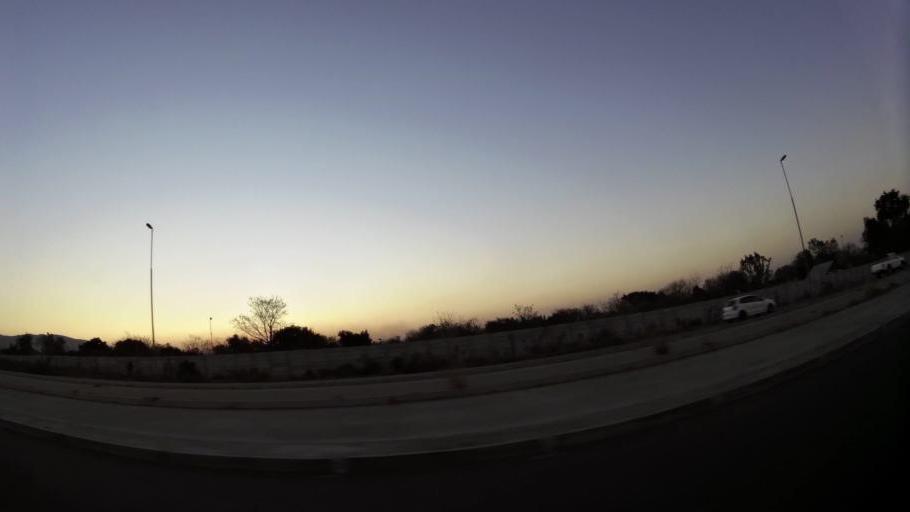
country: ZA
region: North-West
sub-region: Bojanala Platinum District Municipality
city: Rustenburg
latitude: -25.6501
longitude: 27.2518
